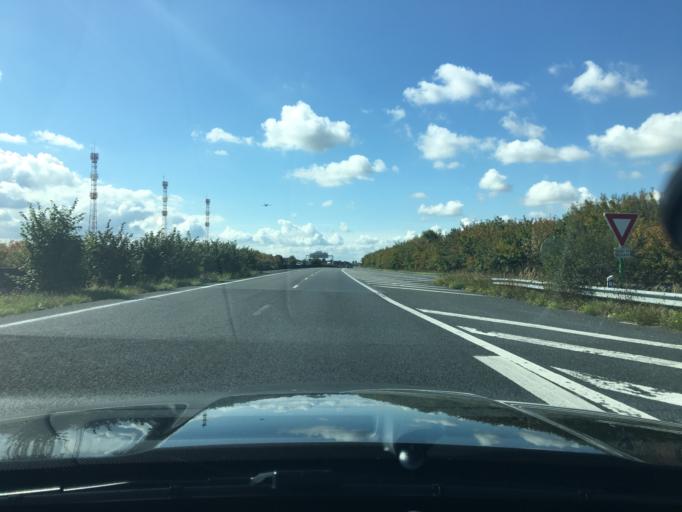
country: FR
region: Ile-de-France
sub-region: Departement du Val-d'Oise
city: Roissy-en-France
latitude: 49.0288
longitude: 2.5275
